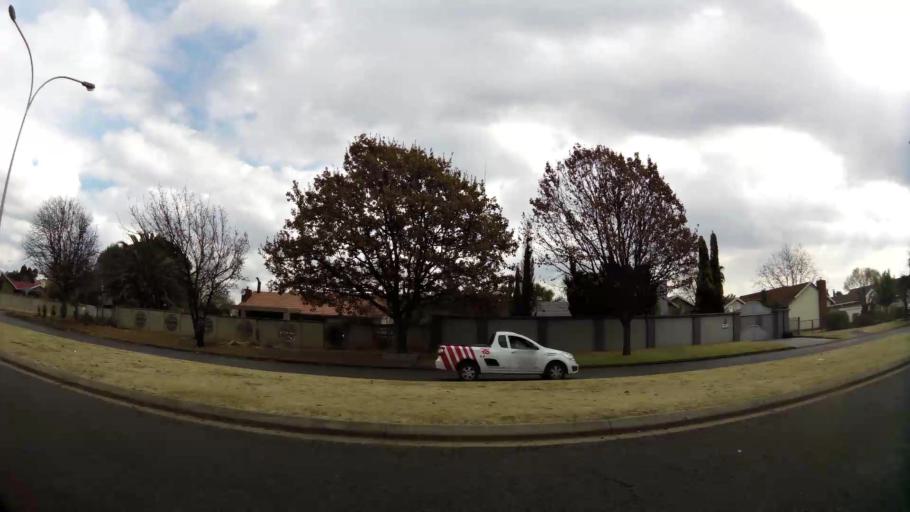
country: ZA
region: Gauteng
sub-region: Sedibeng District Municipality
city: Vanderbijlpark
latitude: -26.7287
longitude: 27.8532
